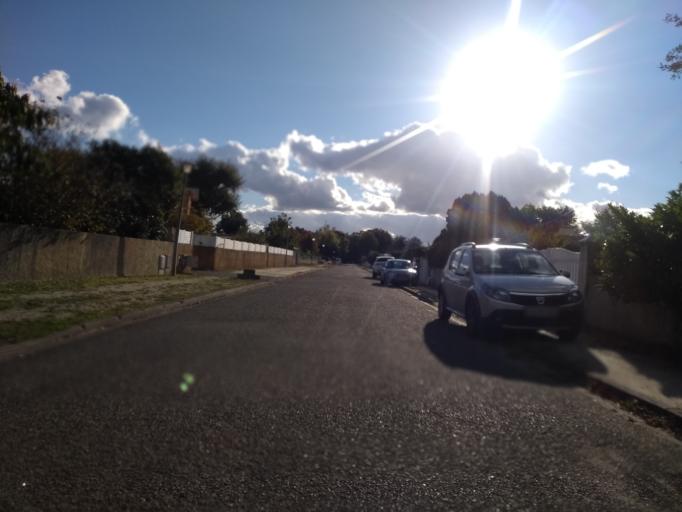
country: FR
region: Aquitaine
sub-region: Departement de la Gironde
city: Cestas
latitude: 44.7180
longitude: -0.6884
